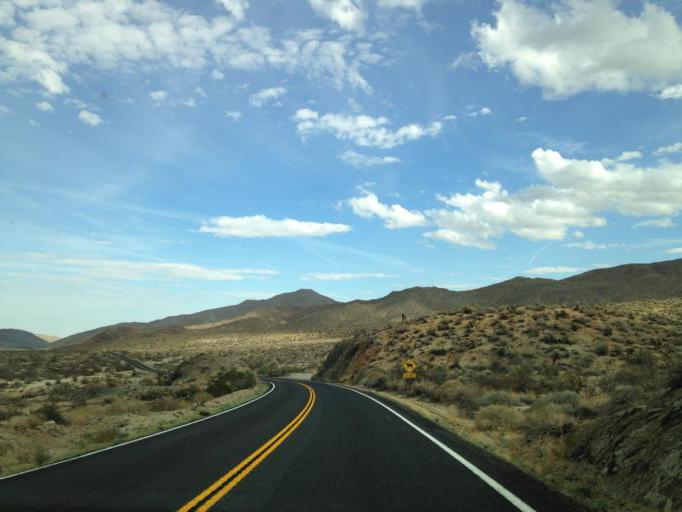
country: US
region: California
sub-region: San Diego County
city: Borrego Springs
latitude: 33.1285
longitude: -116.4295
